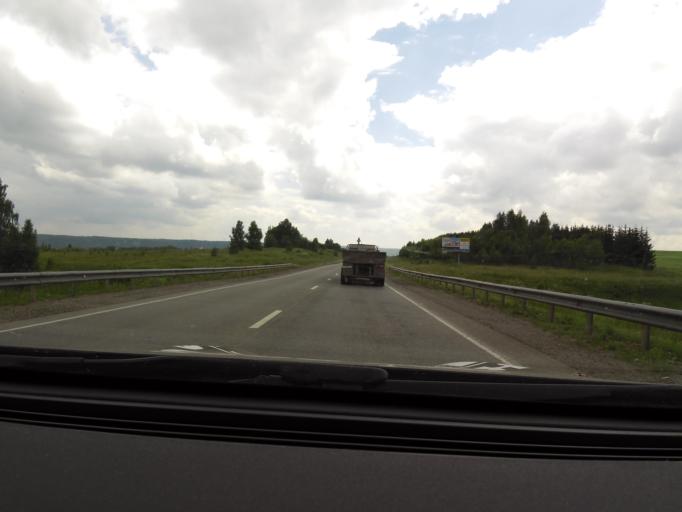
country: RU
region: Perm
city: Kungur
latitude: 57.3920
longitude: 56.9023
